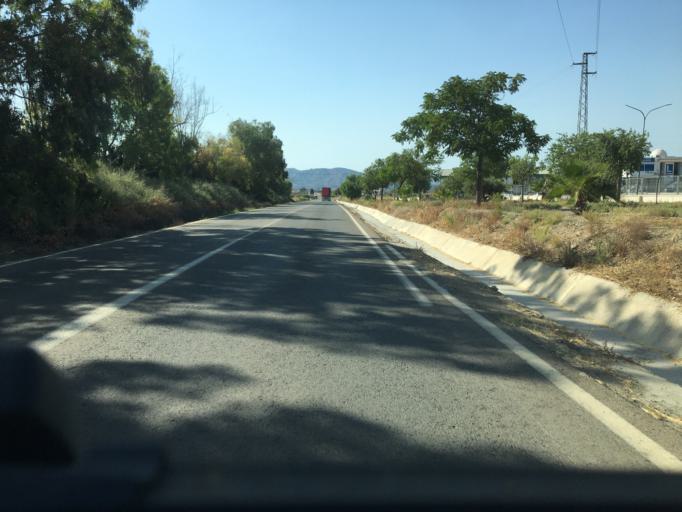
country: ES
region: Andalusia
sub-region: Provincia de Almeria
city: Huercal-Overa
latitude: 37.4140
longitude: -1.9645
